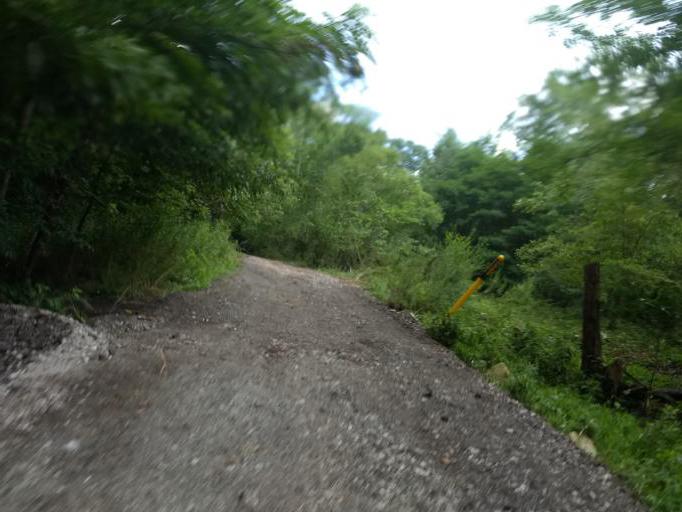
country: US
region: Pennsylvania
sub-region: Allegheny County
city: Swissvale
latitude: 40.4268
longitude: -79.8970
